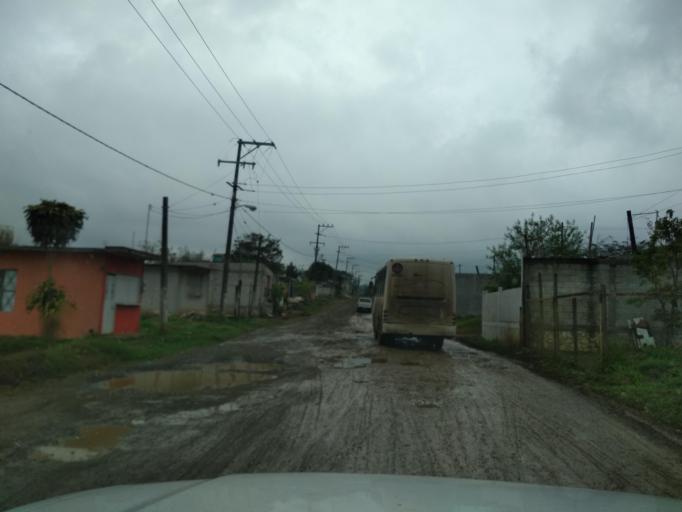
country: MX
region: Veracruz
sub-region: Cordoba
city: San Jose de Tapia
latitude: 18.8484
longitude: -96.9681
